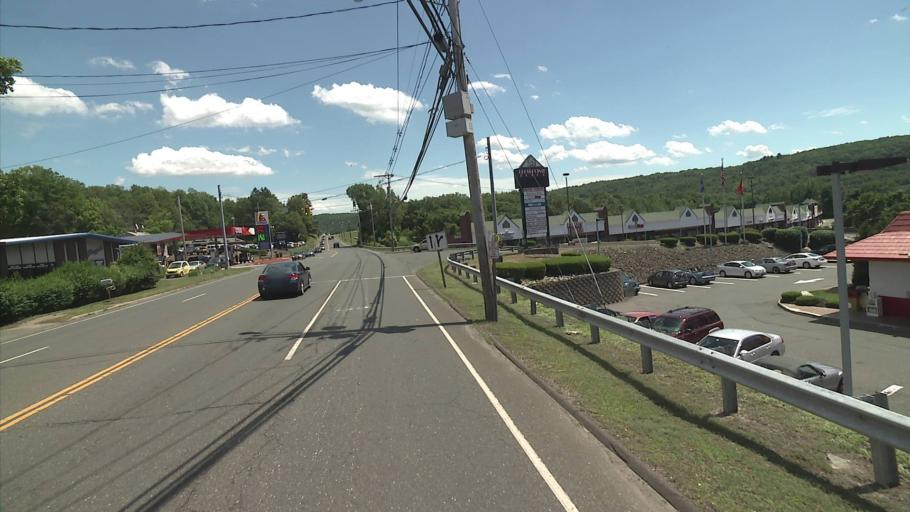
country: US
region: Connecticut
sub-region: New Haven County
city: Naugatuck
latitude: 41.4746
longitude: -73.0429
